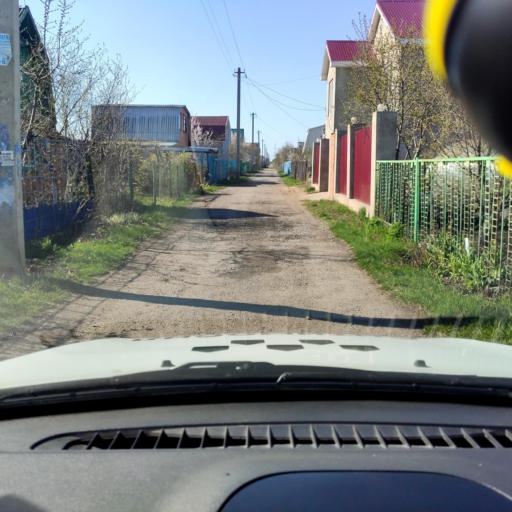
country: RU
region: Samara
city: Tol'yatti
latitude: 53.5991
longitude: 49.2952
